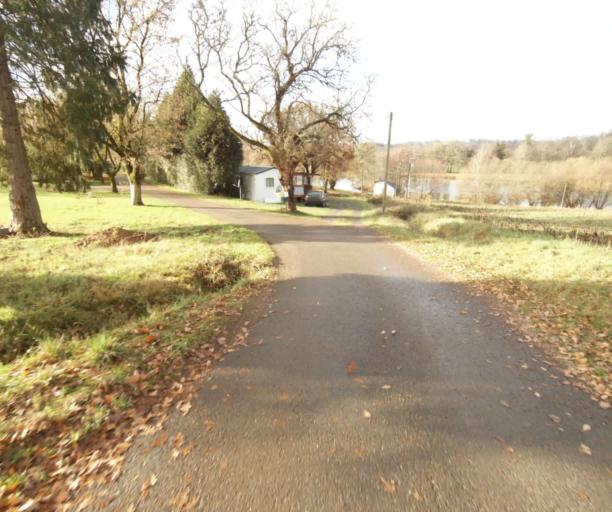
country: FR
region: Limousin
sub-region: Departement de la Correze
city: Sainte-Fereole
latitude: 45.2742
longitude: 1.5969
